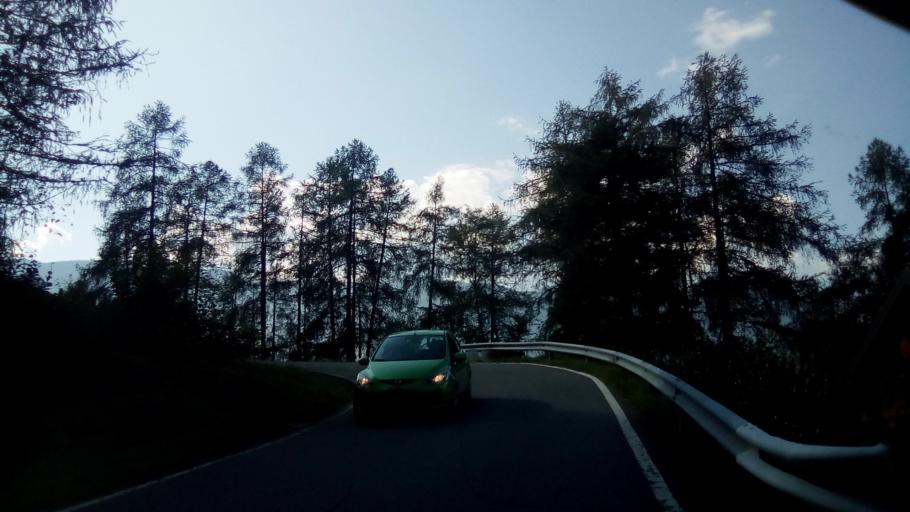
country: CH
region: Valais
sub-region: Martigny District
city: Martigny-Combe
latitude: 46.0676
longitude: 7.0747
